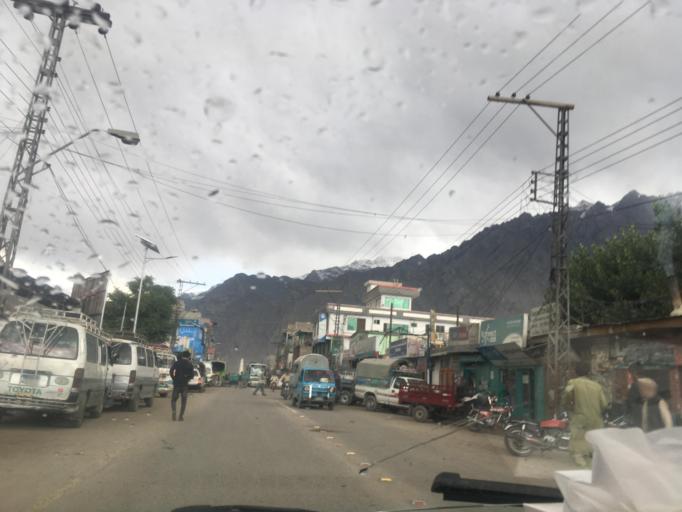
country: PK
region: Gilgit-Baltistan
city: Skardu
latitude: 35.3017
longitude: 75.6275
